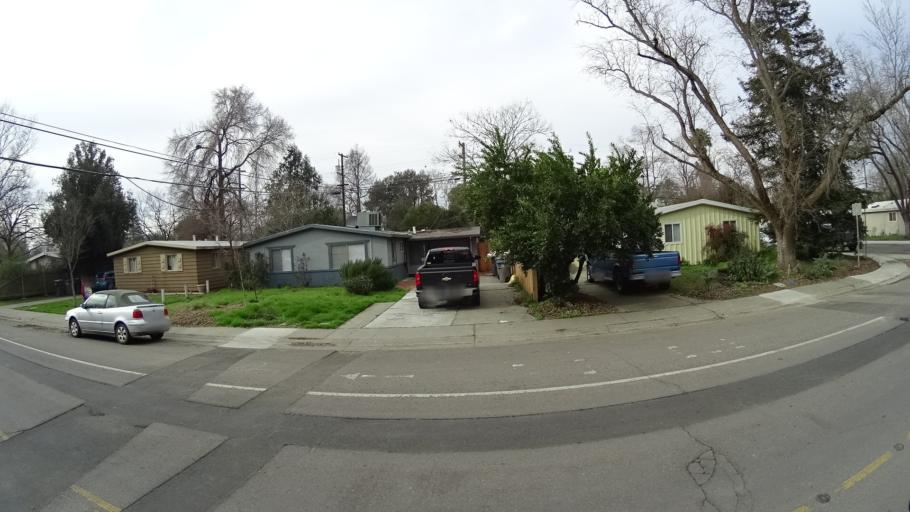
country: US
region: California
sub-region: Yolo County
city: Davis
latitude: 38.5515
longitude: -121.7346
